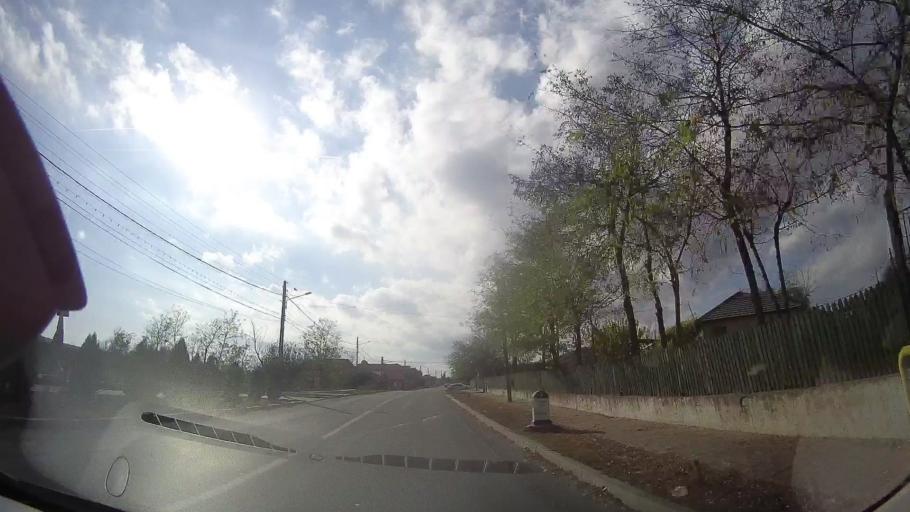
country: RO
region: Constanta
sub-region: Comuna Douazeci si Trei August
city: Dulcesti
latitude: 43.9065
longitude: 28.5472
